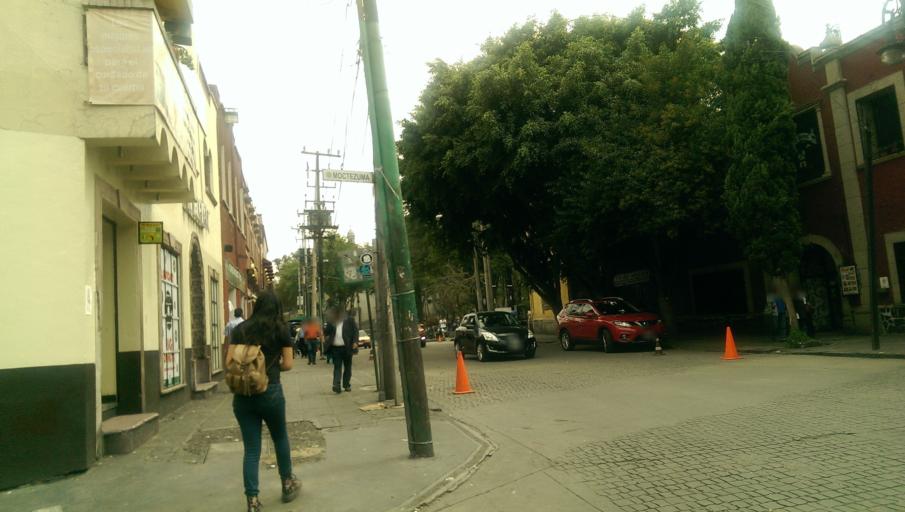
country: MX
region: Mexico City
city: Coyoacan
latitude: 19.3506
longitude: -99.1616
